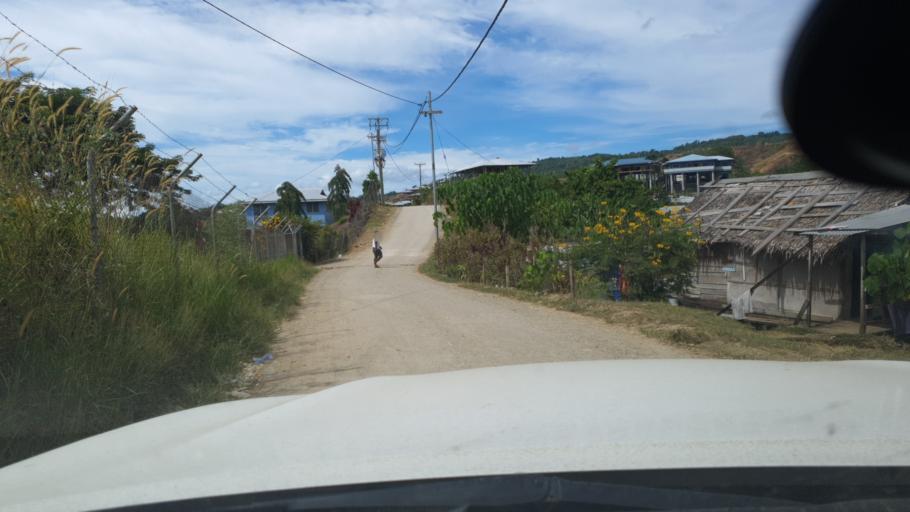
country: SB
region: Guadalcanal
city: Honiara
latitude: -9.4473
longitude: 159.9733
